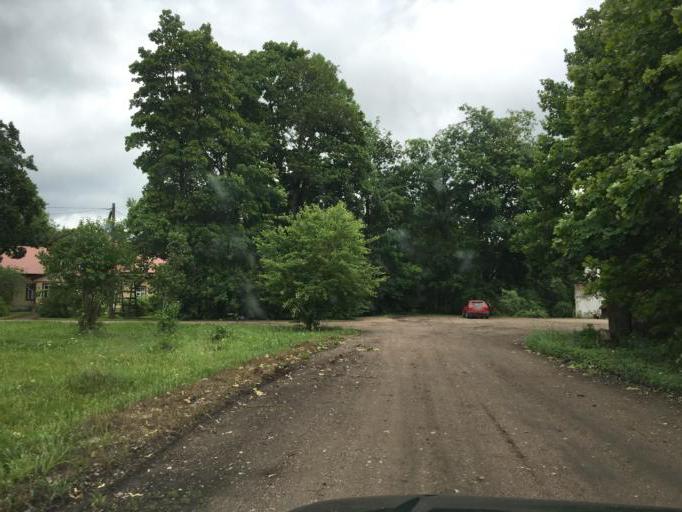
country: LV
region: Vilaka
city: Vilaka
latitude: 57.3471
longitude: 27.4683
